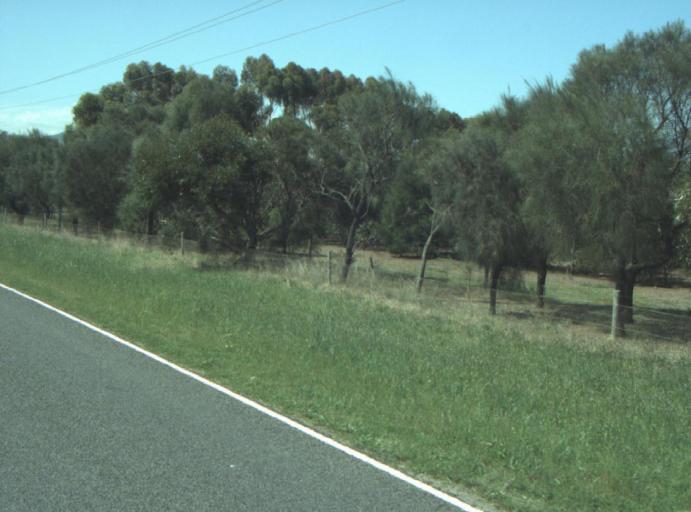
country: AU
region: Victoria
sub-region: Greater Geelong
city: Lara
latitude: -37.9953
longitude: 144.4013
